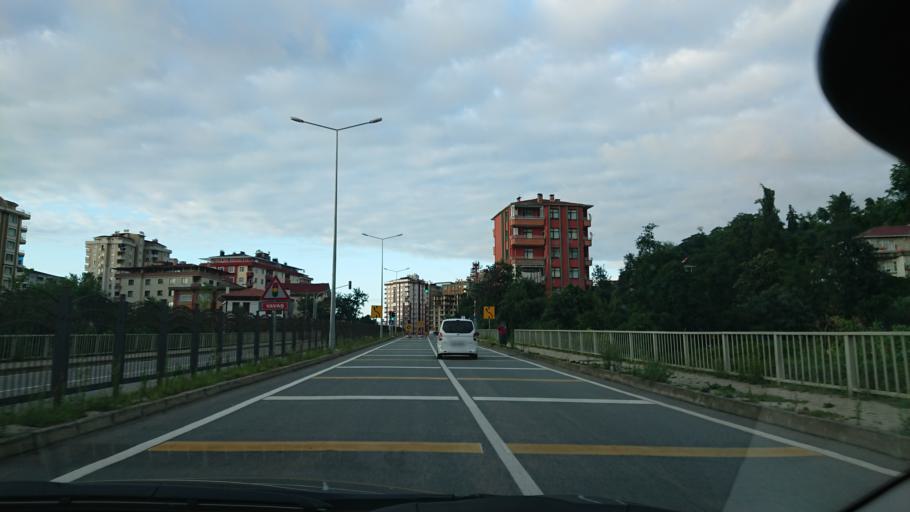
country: TR
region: Rize
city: Gundogdu
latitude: 41.0344
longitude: 40.5638
